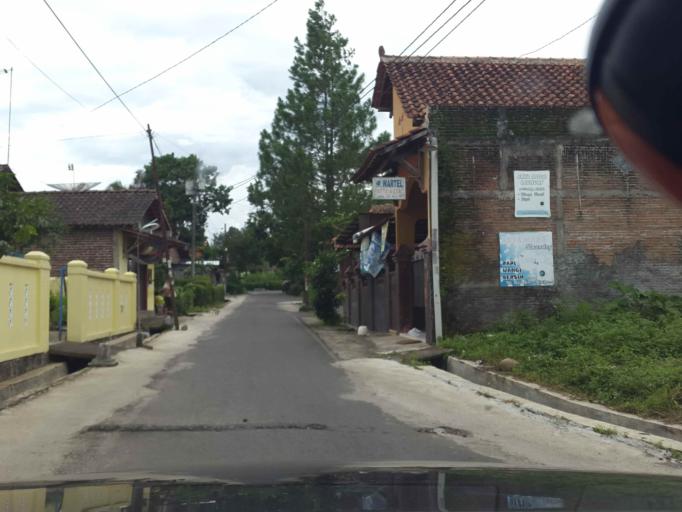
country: ID
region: Central Java
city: Salatiga
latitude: -7.3364
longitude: 110.4900
